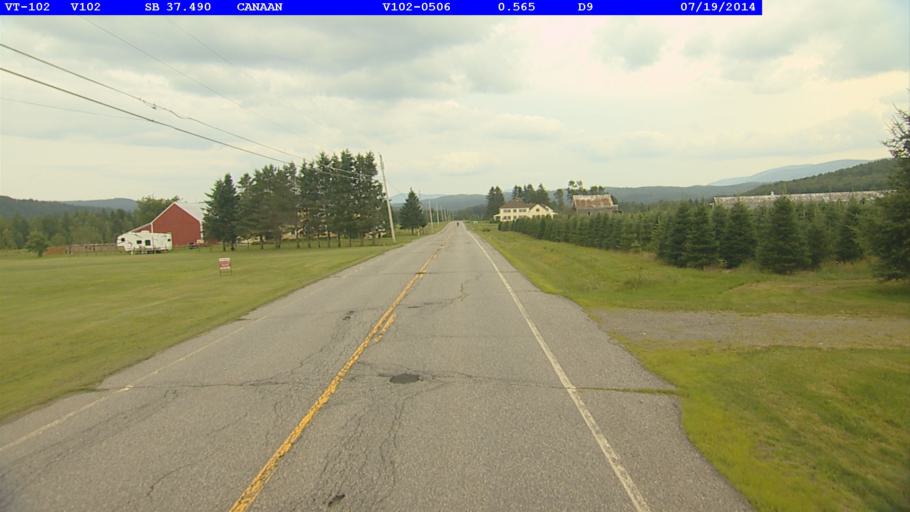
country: US
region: New Hampshire
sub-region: Coos County
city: Colebrook
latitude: 44.9172
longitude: -71.5141
